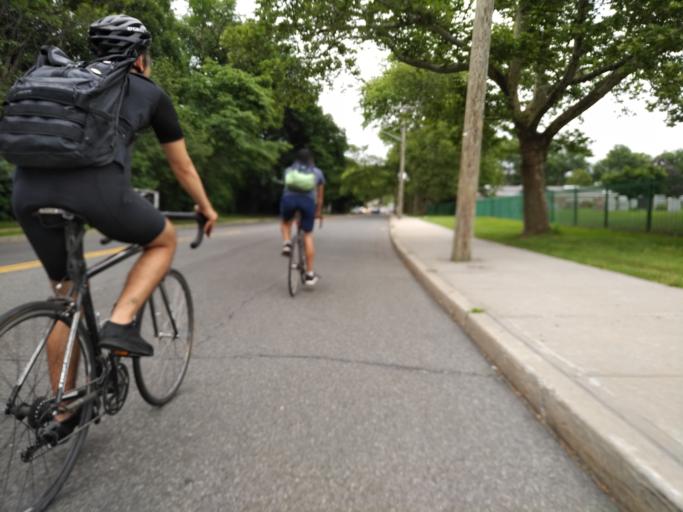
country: US
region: New York
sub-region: Queens County
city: Jamaica
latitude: 40.7422
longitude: -73.7996
